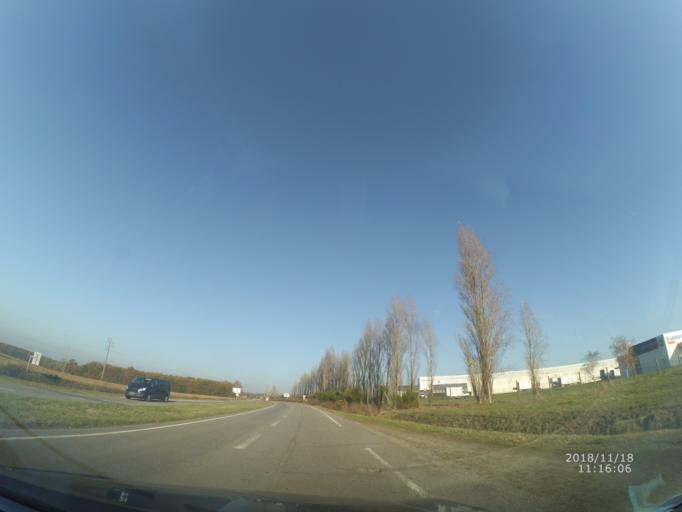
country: FR
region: Pays de la Loire
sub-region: Departement de la Loire-Atlantique
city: Saint-Pere-en-Retz
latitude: 47.2124
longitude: -2.0526
